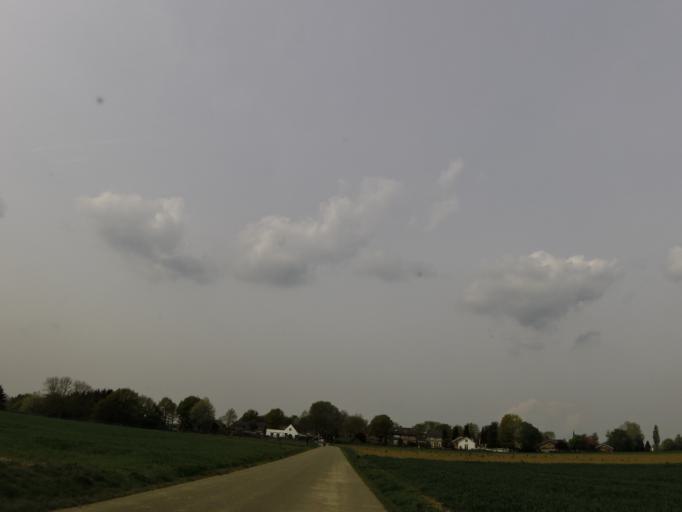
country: NL
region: Limburg
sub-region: Gemeente Kerkrade
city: Kerkrade
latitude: 50.9130
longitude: 6.0653
